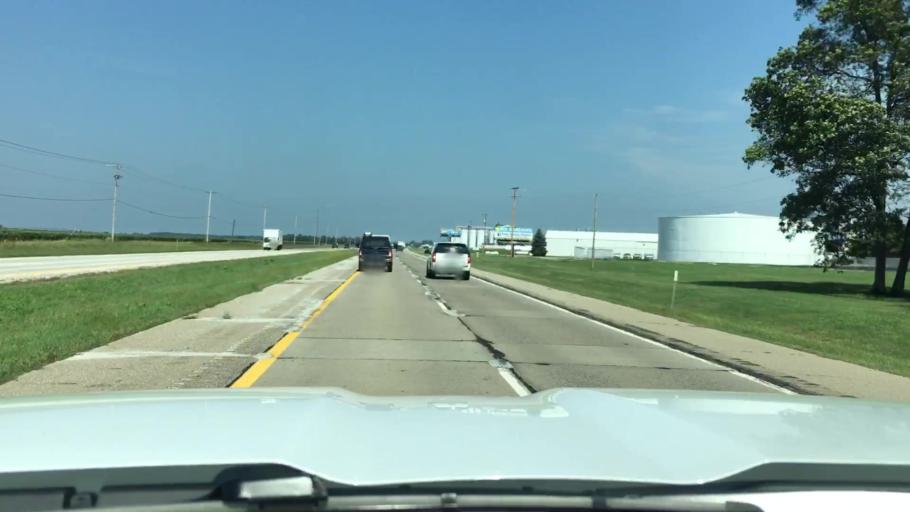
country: US
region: Michigan
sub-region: Kalamazoo County
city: Schoolcraft
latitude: 42.0710
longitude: -85.6364
